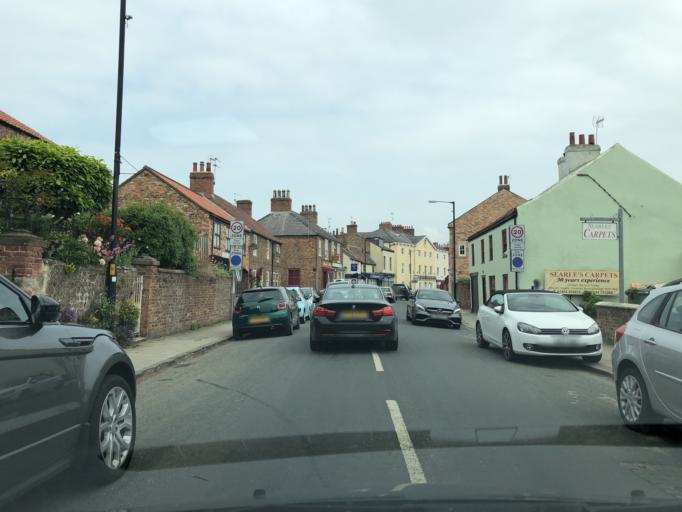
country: GB
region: England
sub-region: North Yorkshire
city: Boroughbridge
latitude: 54.0954
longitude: -1.3973
